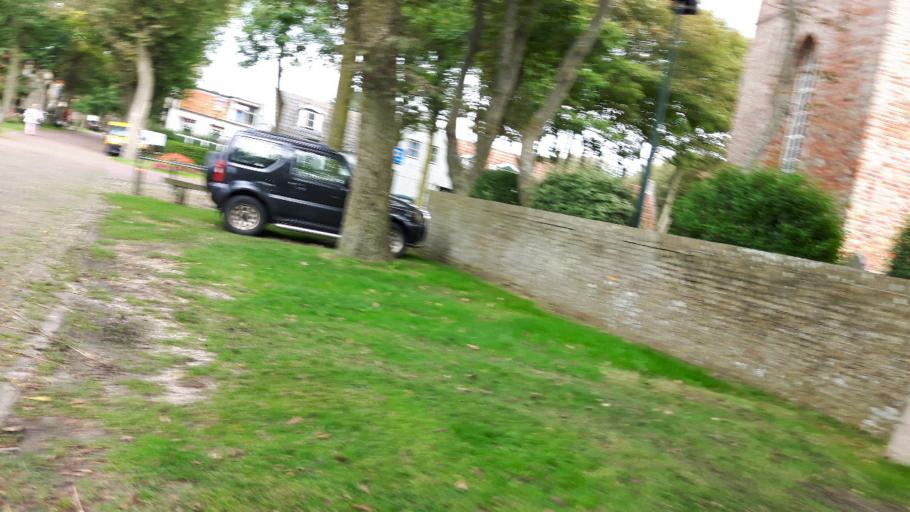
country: NL
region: Friesland
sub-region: Gemeente Ameland
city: Hollum
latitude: 53.4356
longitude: 5.6405
